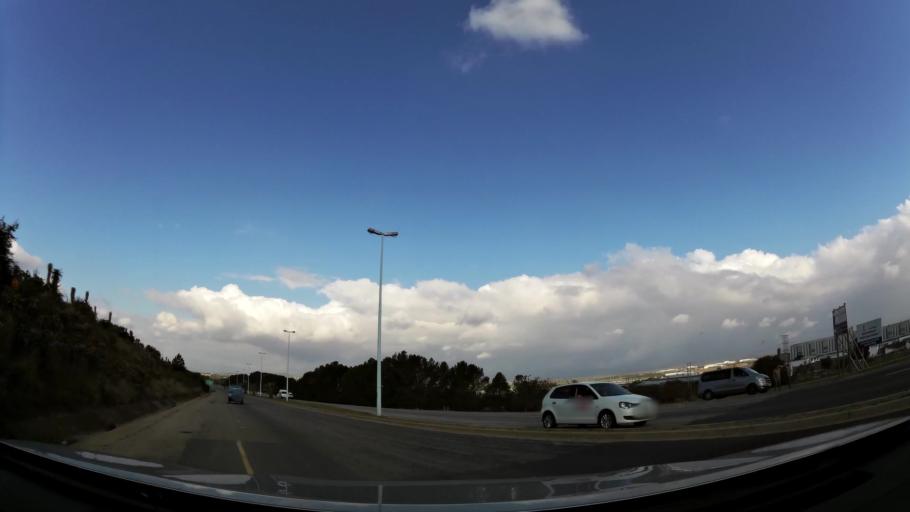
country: ZA
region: Eastern Cape
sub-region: Nelson Mandela Bay Metropolitan Municipality
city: Uitenhage
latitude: -33.7803
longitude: 25.4239
